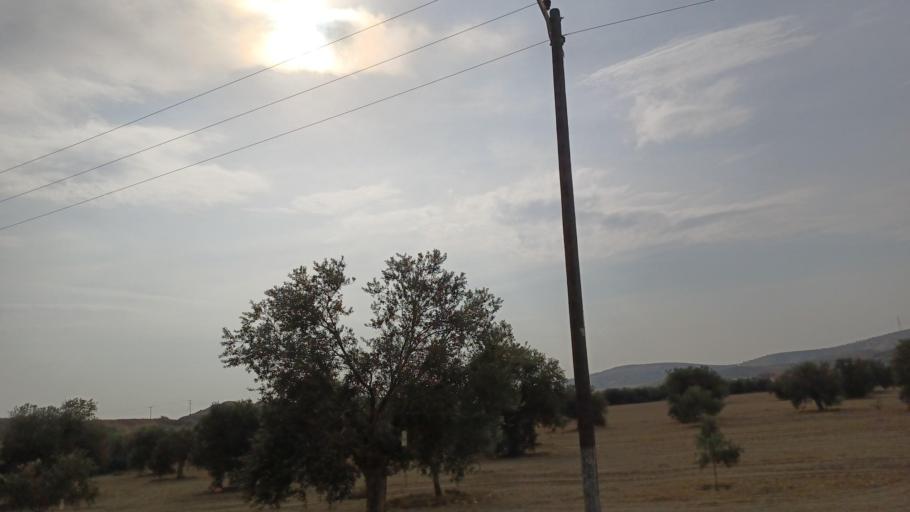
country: CY
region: Larnaka
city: Troulloi
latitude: 35.0102
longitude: 33.5724
